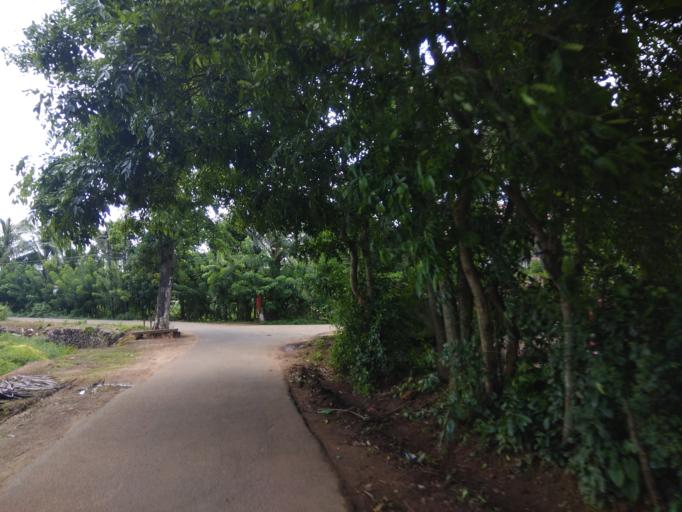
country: IN
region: Kerala
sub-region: Thrissur District
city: Trichur
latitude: 10.5428
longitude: 76.1682
